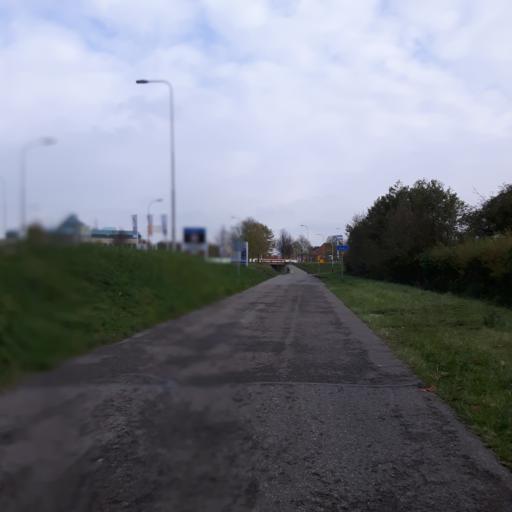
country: NL
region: Zeeland
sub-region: Gemeente Goes
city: Goes
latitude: 51.5053
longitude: 3.8743
